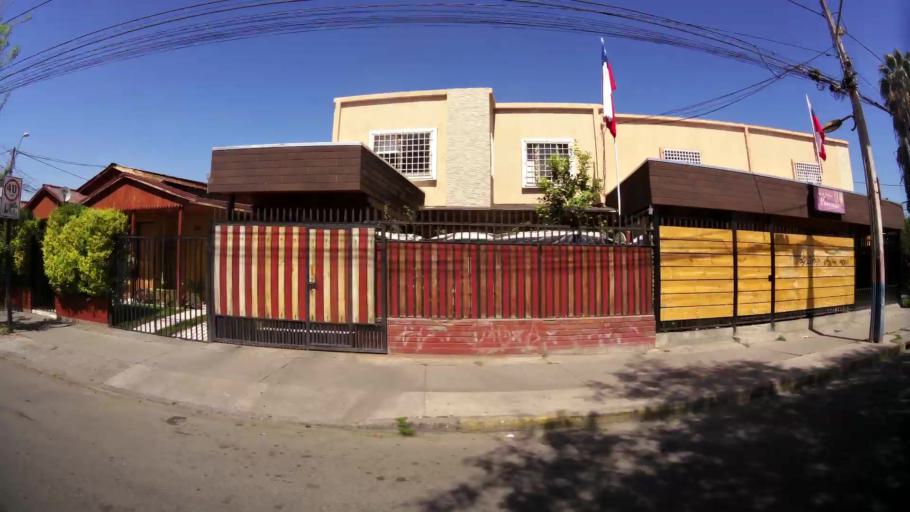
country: CL
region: Santiago Metropolitan
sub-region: Provincia de Santiago
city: Lo Prado
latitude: -33.4910
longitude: -70.7382
